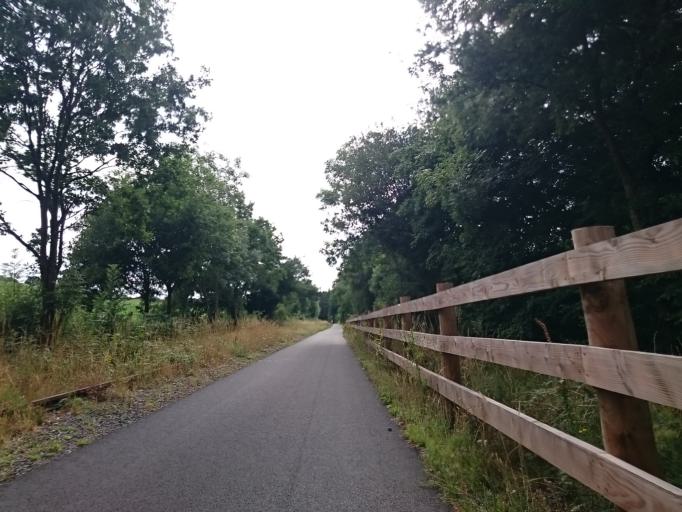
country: FR
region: Lower Normandy
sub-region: Departement du Calvados
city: Thury-Harcourt
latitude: 48.9999
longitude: -0.4709
